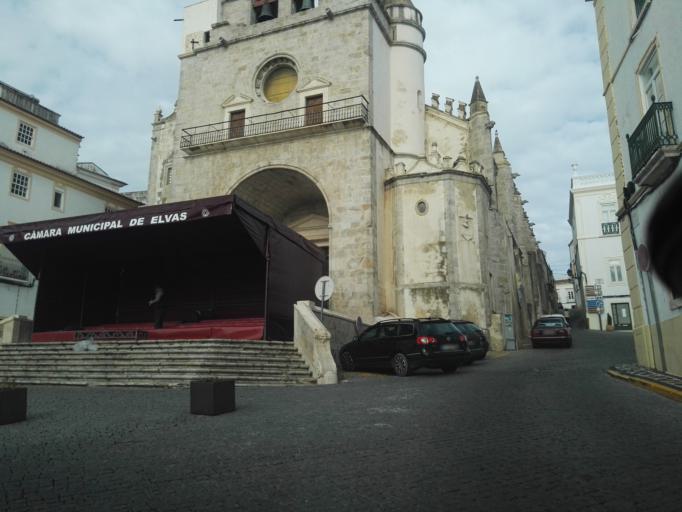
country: PT
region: Portalegre
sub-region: Elvas
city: Elvas
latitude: 38.8809
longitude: -7.1637
